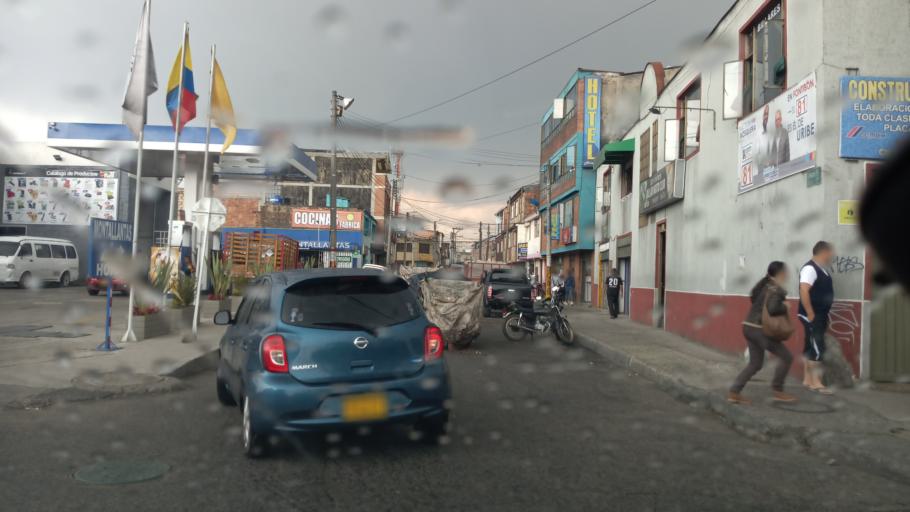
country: CO
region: Cundinamarca
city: Funza
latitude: 4.6698
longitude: -74.1436
